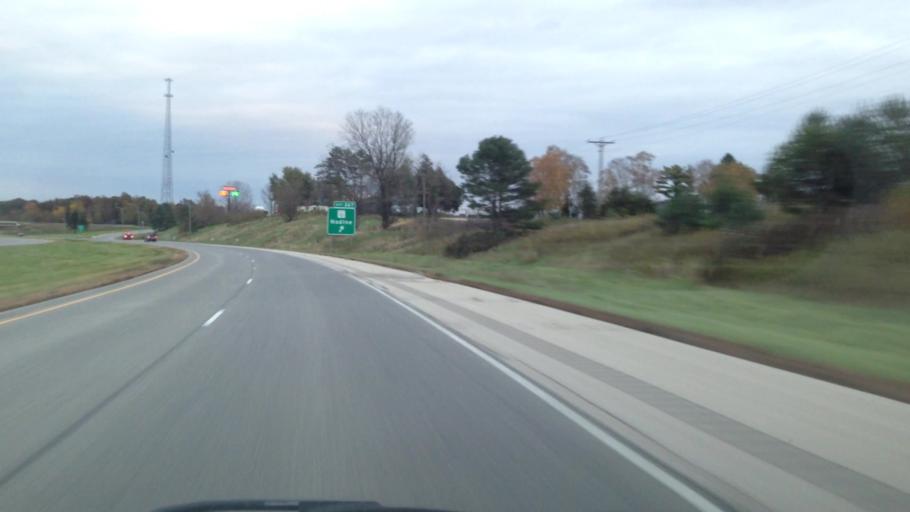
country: US
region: Wisconsin
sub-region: Trempealeau County
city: Trempealeau
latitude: 43.9225
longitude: -91.4442
